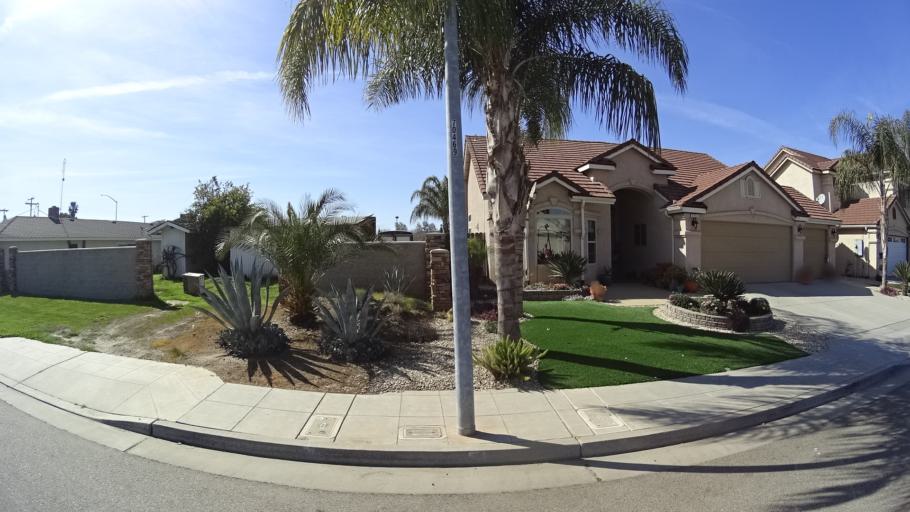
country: US
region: California
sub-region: Fresno County
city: Clovis
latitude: 36.8454
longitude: -119.7337
